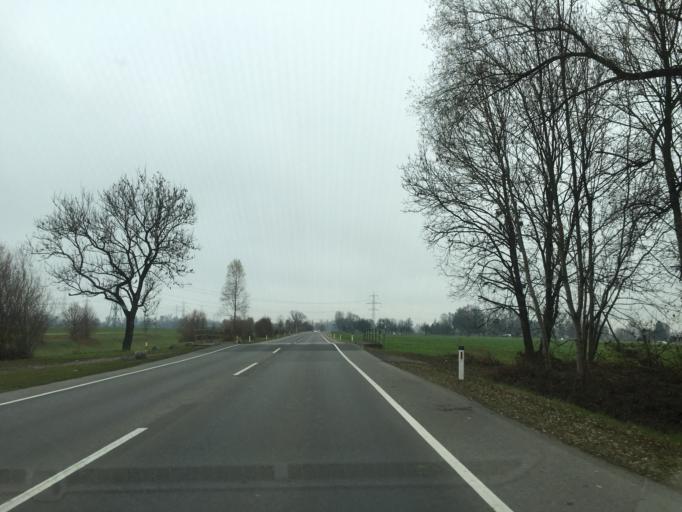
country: AT
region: Vorarlberg
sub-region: Politischer Bezirk Dornbirn
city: Hohenems
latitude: 47.3815
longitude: 9.6808
